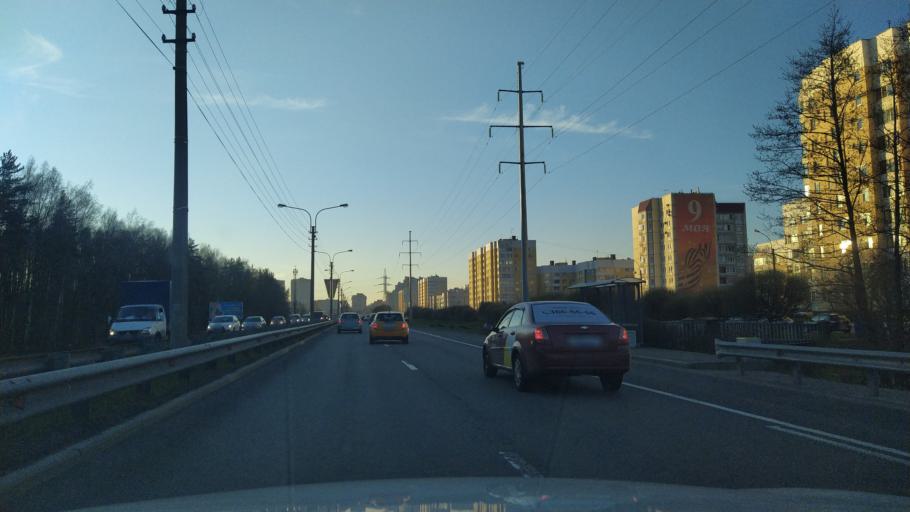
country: RU
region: St.-Petersburg
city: Razliv
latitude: 60.0763
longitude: 29.9642
